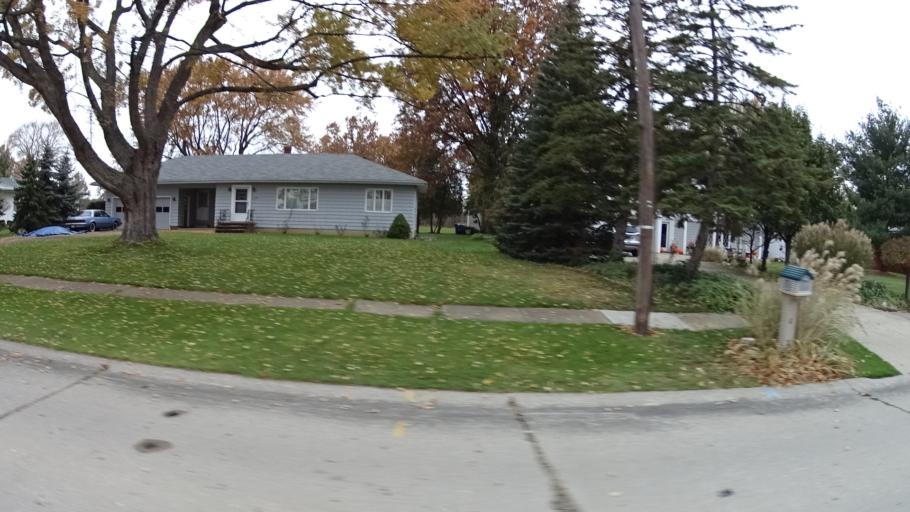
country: US
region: Ohio
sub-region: Lorain County
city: Lorain
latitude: 41.4387
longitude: -82.2094
